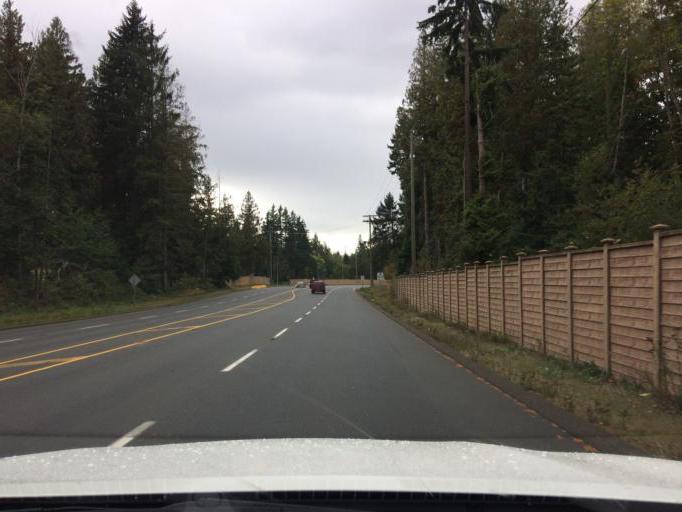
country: CA
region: British Columbia
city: Courtenay
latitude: 49.7168
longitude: -124.9860
